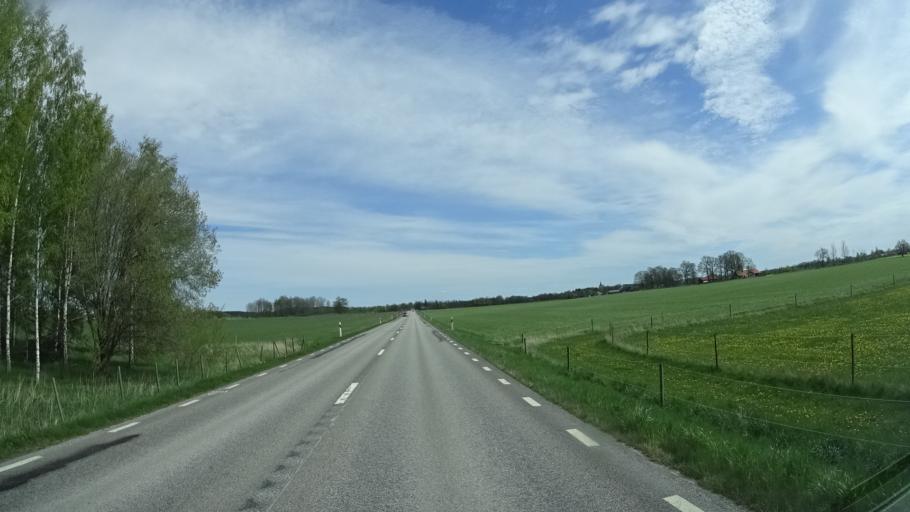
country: SE
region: OEstergoetland
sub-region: Mjolby Kommun
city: Mantorp
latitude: 58.3698
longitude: 15.3520
